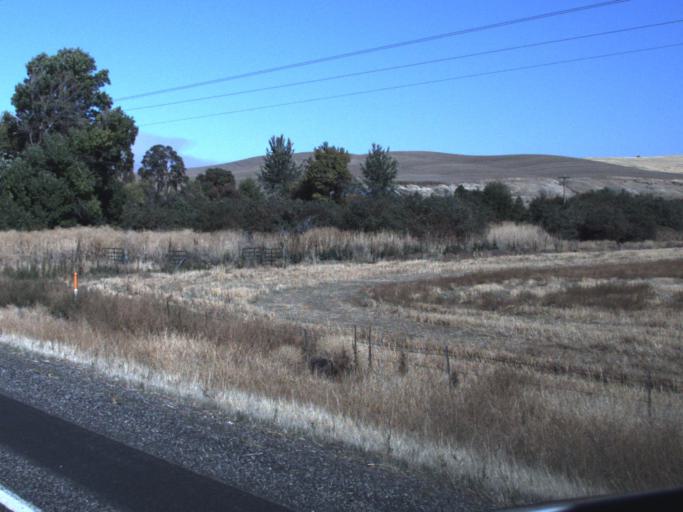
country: US
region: Washington
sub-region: Walla Walla County
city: Waitsburg
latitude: 46.2725
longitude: -118.2211
